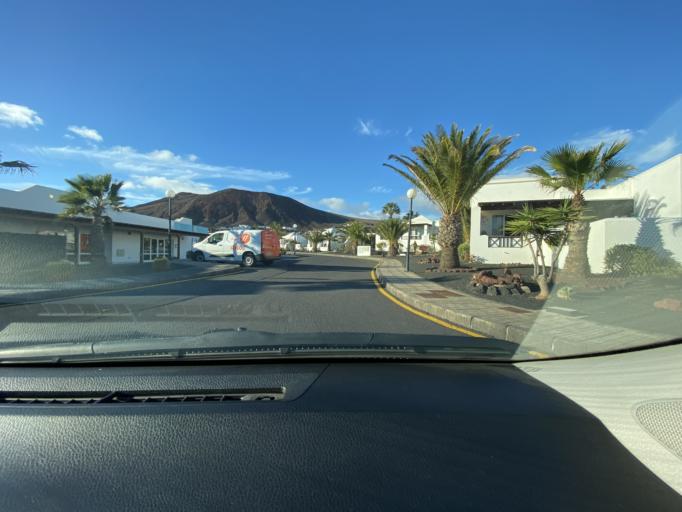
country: ES
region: Canary Islands
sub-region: Provincia de Las Palmas
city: Playa Blanca
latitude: 28.8641
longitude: -13.8477
